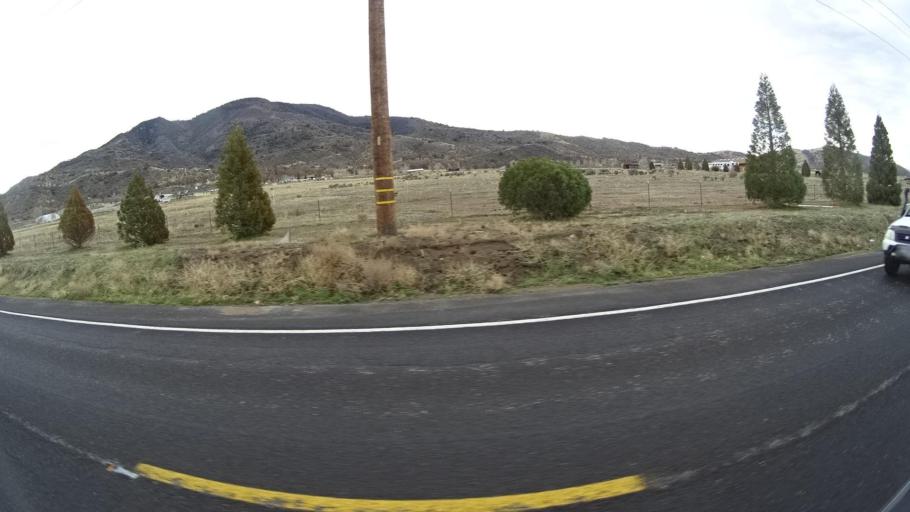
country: US
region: California
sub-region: Kern County
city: Stallion Springs
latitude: 35.0953
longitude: -118.6062
